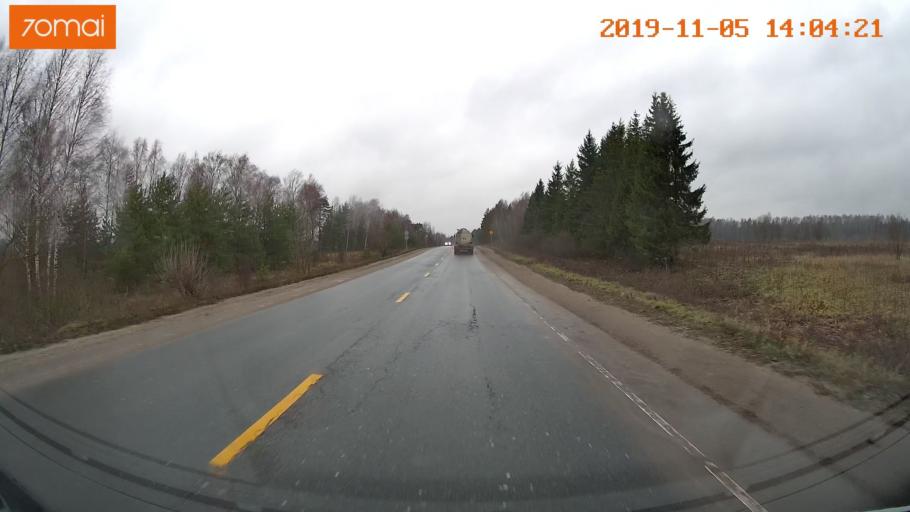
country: RU
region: Ivanovo
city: Kokhma
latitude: 56.9973
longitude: 41.1777
